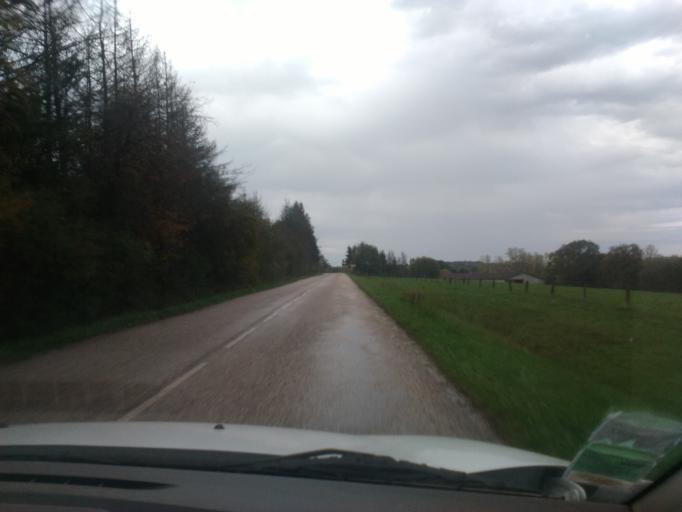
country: FR
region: Lorraine
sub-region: Departement des Vosges
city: Dogneville
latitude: 48.2719
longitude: 6.4919
